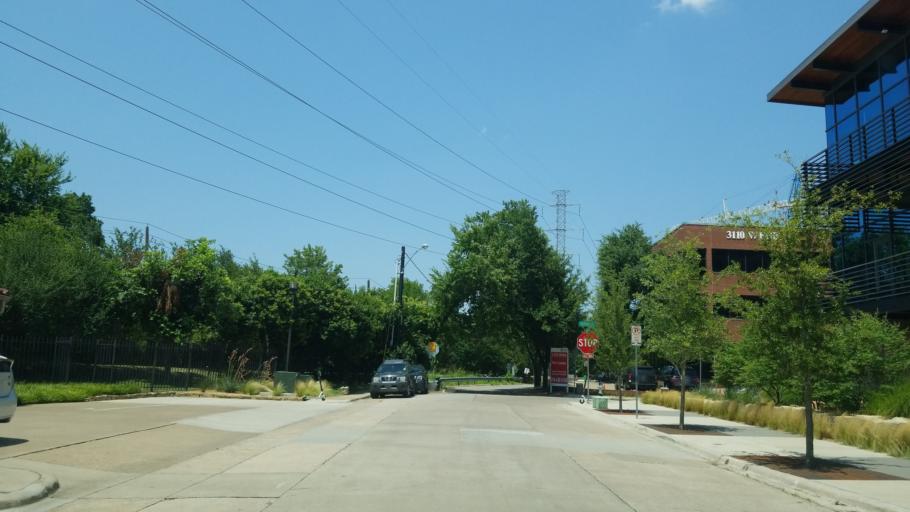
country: US
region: Texas
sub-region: Dallas County
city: Highland Park
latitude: 32.8289
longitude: -96.7851
